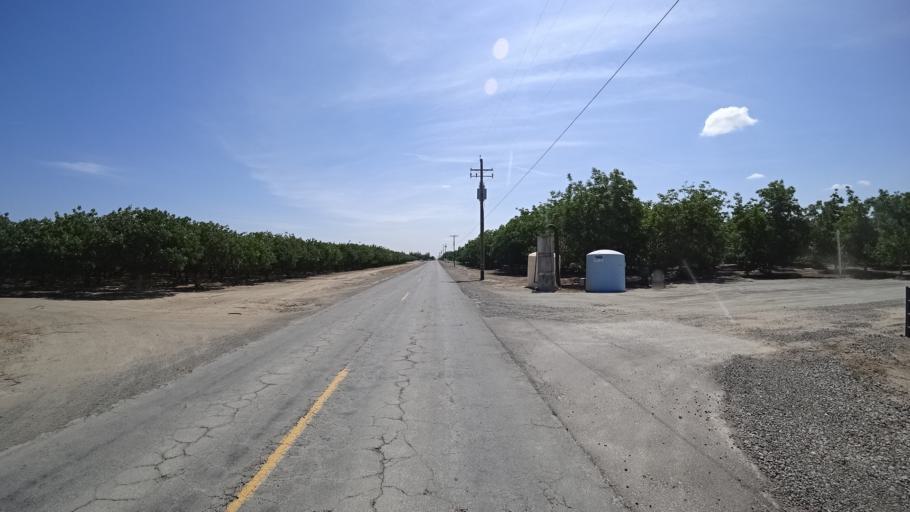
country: US
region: California
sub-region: Kings County
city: Armona
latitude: 36.2693
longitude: -119.7003
